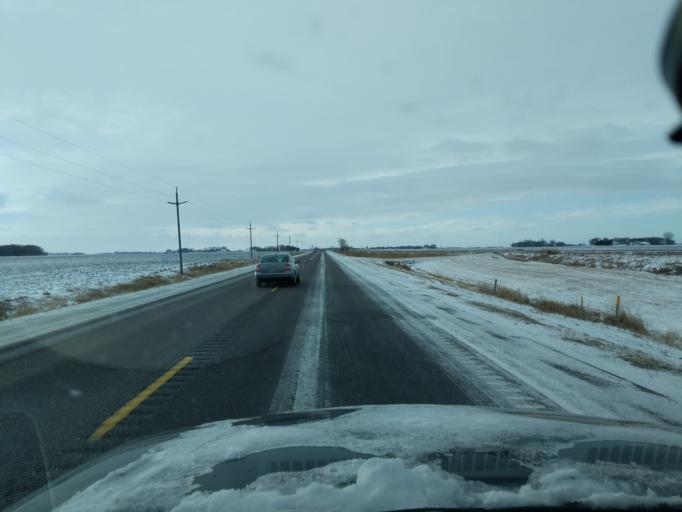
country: US
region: Minnesota
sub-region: McLeod County
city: Hutchinson
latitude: 44.7245
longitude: -94.4301
